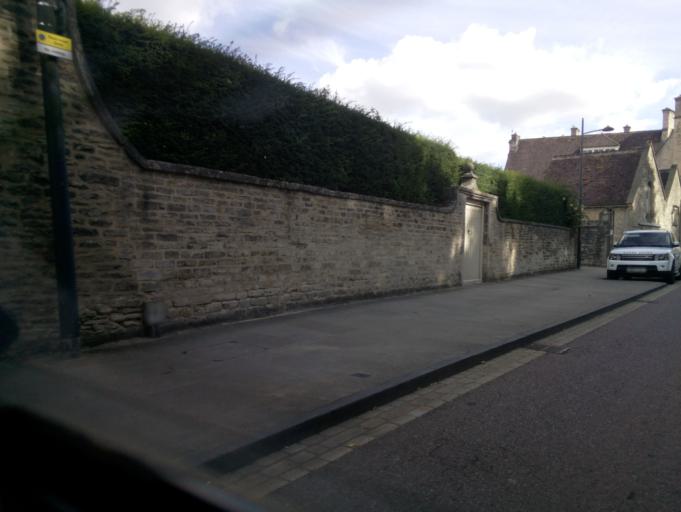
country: GB
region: England
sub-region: Gloucestershire
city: Cirencester
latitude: 51.7167
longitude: -1.9713
